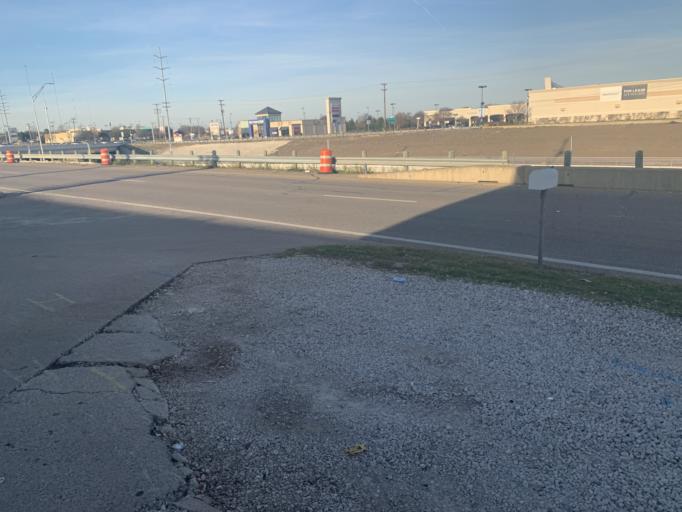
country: US
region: Texas
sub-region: Dallas County
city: Cedar Hill
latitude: 32.6052
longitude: -96.9297
